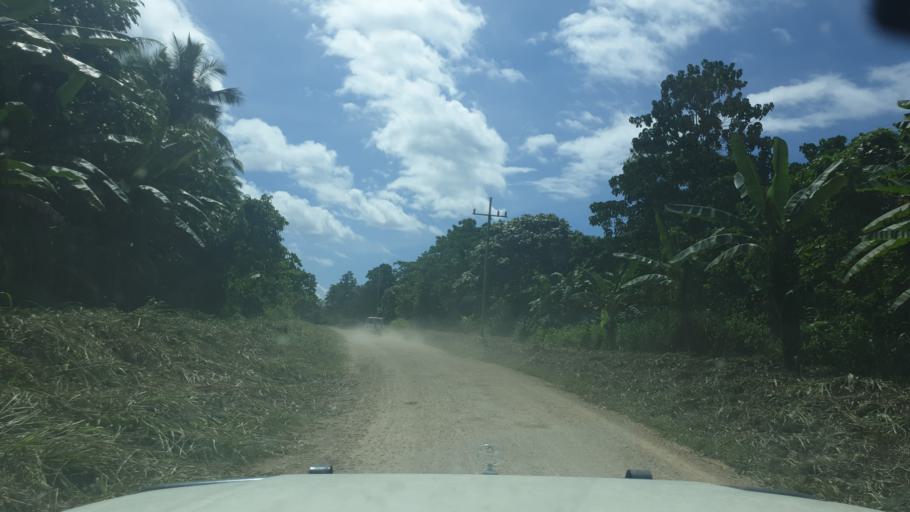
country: PG
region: Bougainville
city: Buka
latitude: -5.5201
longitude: 154.8246
